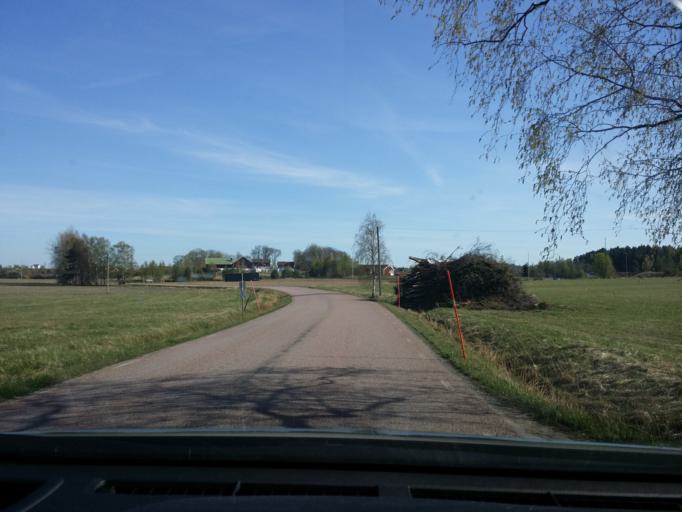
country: SE
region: Vaestmanland
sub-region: Vasteras
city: Vasteras
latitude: 59.6364
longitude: 16.4852
